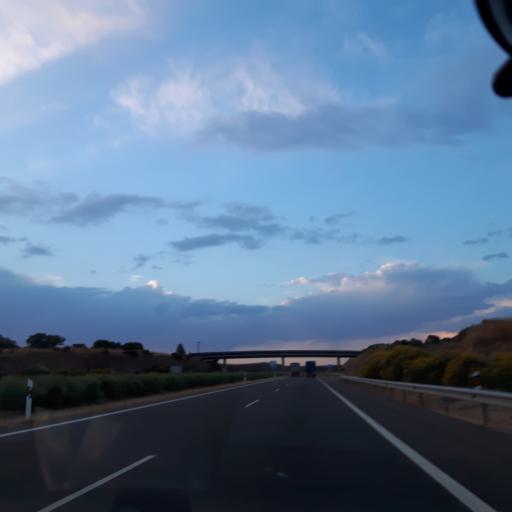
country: ES
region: Castille and Leon
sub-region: Provincia de Salamanca
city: Mozarbez
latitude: 40.8682
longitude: -5.6535
